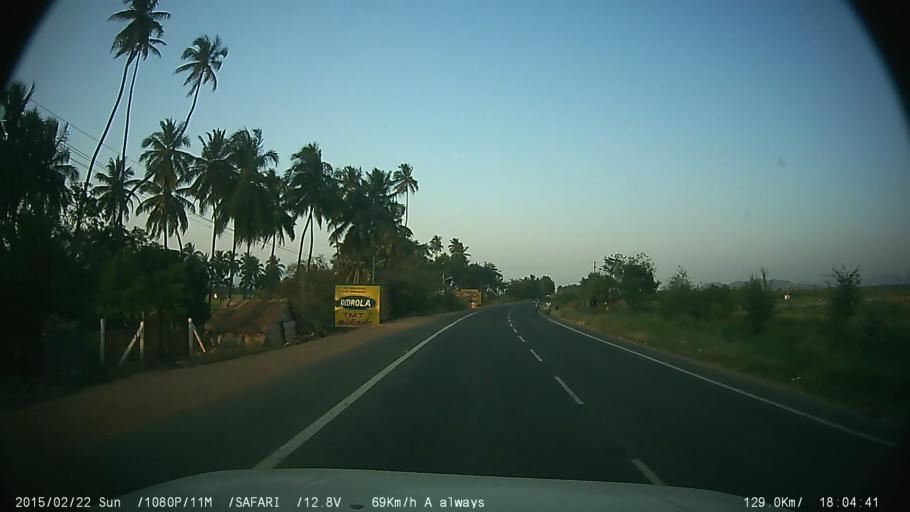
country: IN
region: Tamil Nadu
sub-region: Theni
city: Uttamapalaiyam
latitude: 9.8178
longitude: 77.3512
